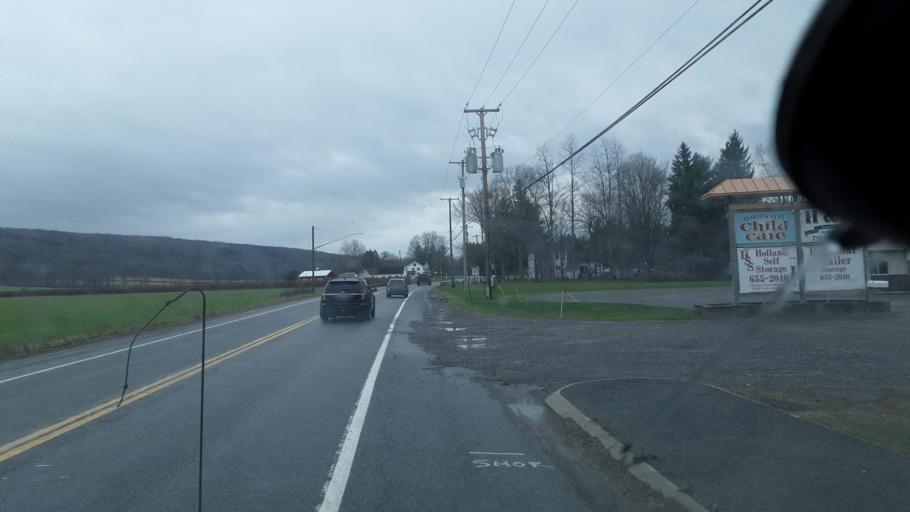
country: US
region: New York
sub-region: Erie County
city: Holland
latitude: 42.6819
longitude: -78.5645
